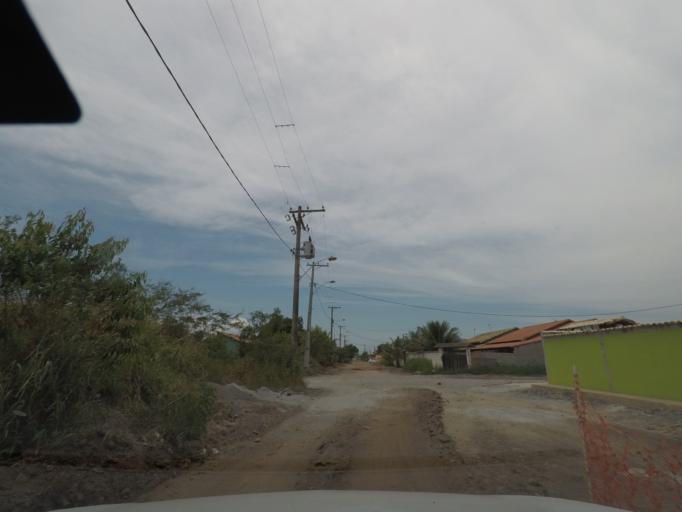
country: BR
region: Rio de Janeiro
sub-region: Marica
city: Marica
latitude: -22.9594
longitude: -42.9517
